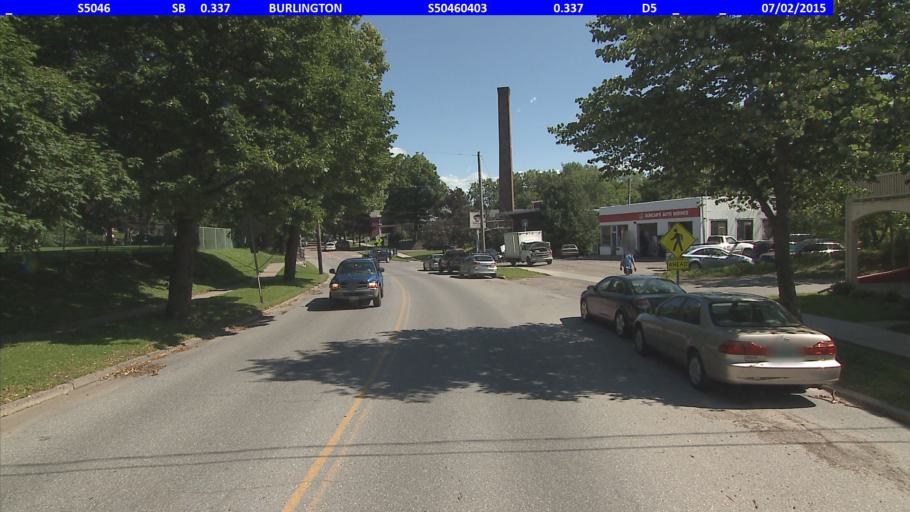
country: US
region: Vermont
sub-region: Chittenden County
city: Burlington
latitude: 44.4717
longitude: -73.2137
